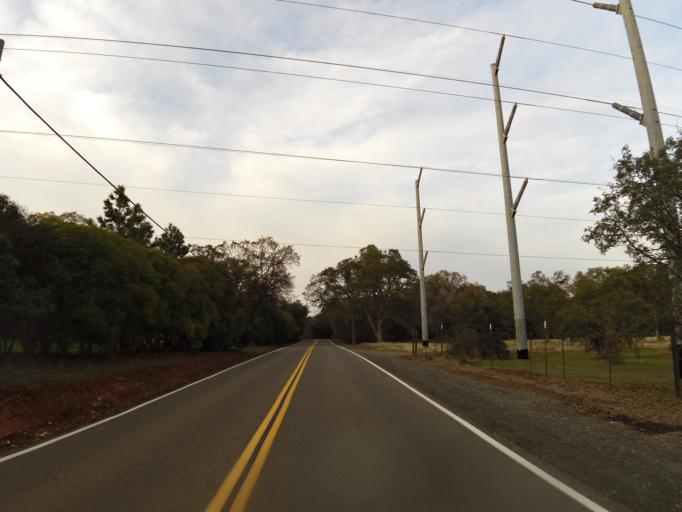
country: US
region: California
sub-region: El Dorado County
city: Cameron Park
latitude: 38.7073
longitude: -121.0038
